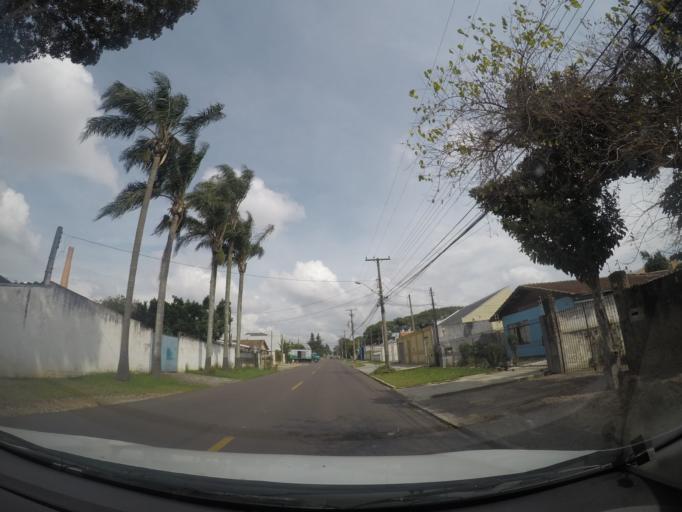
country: BR
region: Parana
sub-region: Curitiba
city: Curitiba
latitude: -25.4789
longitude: -49.2638
